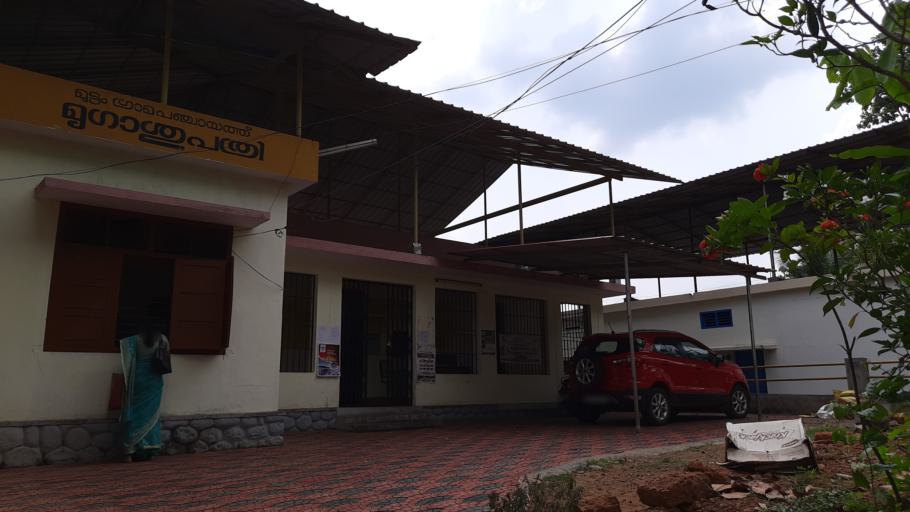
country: IN
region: Kerala
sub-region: Kottayam
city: Lalam
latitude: 9.8348
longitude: 76.7447
